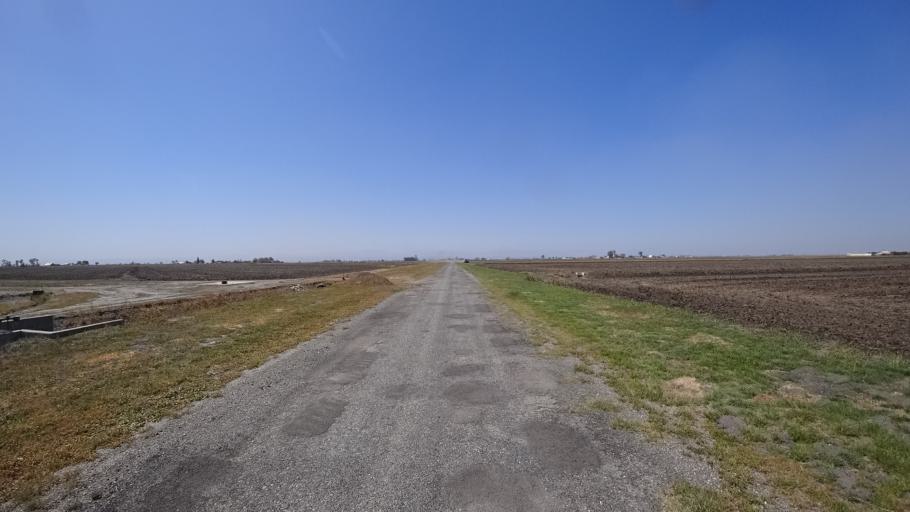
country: US
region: California
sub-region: Glenn County
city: Willows
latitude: 39.5311
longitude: -122.0996
